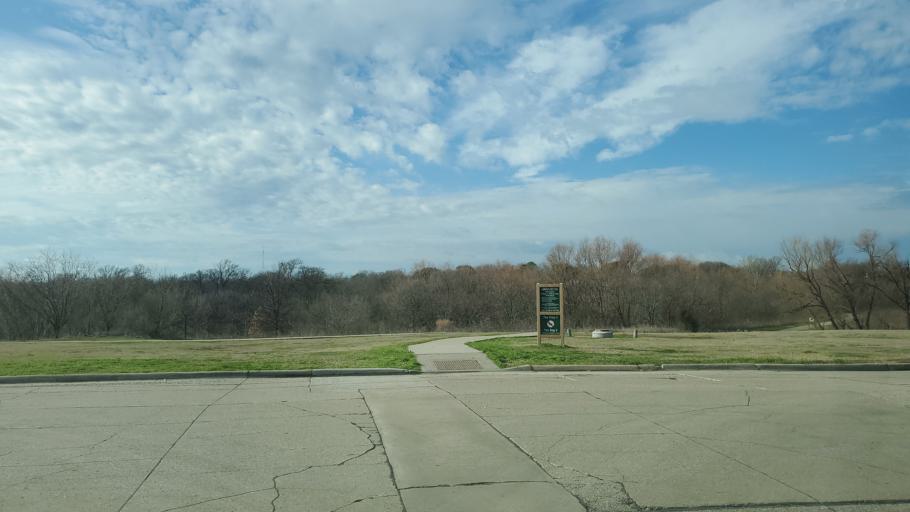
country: US
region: Texas
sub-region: Dallas County
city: Carrollton
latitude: 32.9918
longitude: -96.8956
